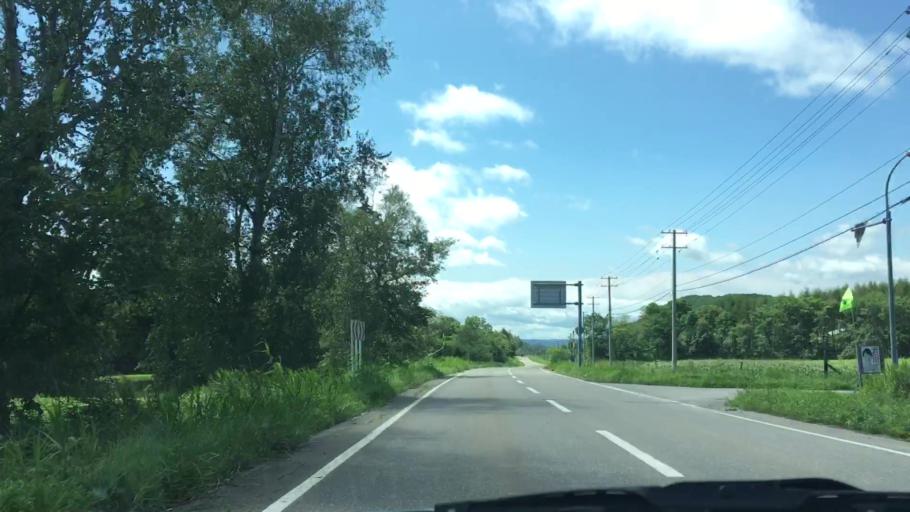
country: JP
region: Hokkaido
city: Kitami
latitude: 43.3008
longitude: 143.6831
